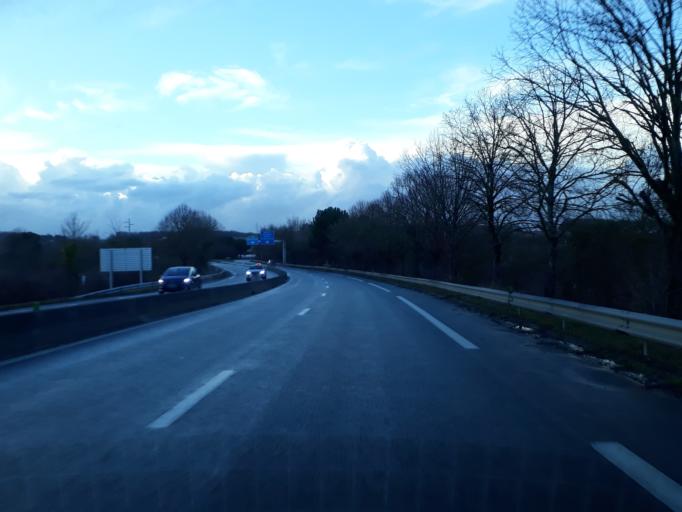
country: FR
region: Poitou-Charentes
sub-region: Departement de la Charente-Maritime
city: Saintes
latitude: 45.7536
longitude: -0.6669
